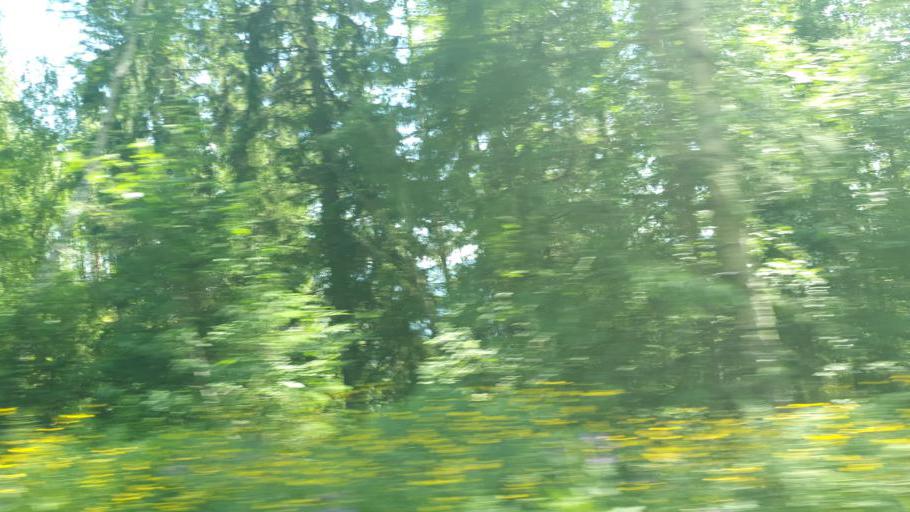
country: NO
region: Nord-Trondelag
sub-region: Frosta
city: Frosta
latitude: 63.6993
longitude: 10.7319
